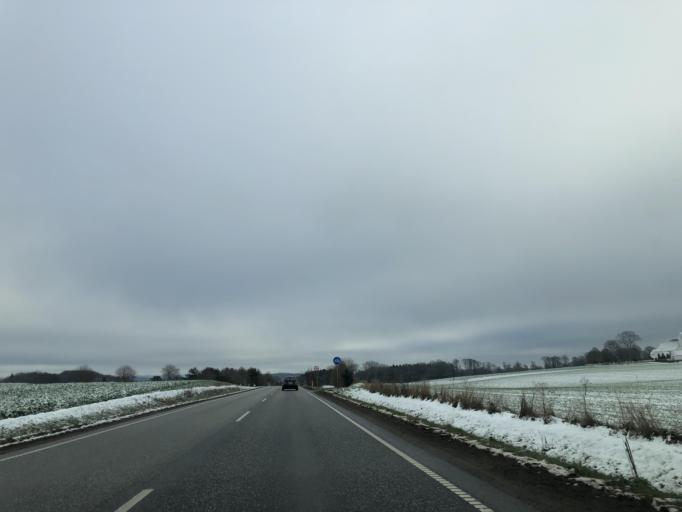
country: DK
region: Central Jutland
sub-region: Horsens Kommune
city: Horsens
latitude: 55.8950
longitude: 9.7317
